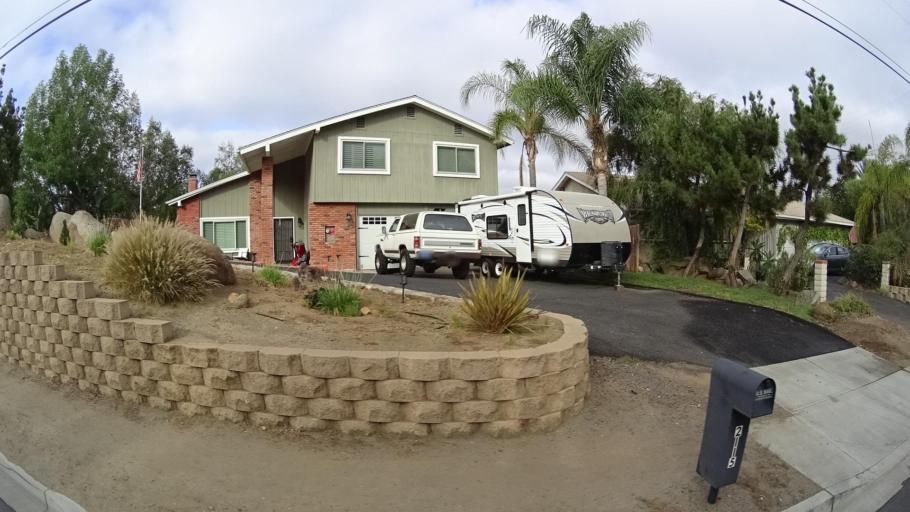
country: US
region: California
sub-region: San Diego County
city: Vista
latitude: 33.2082
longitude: -117.2081
